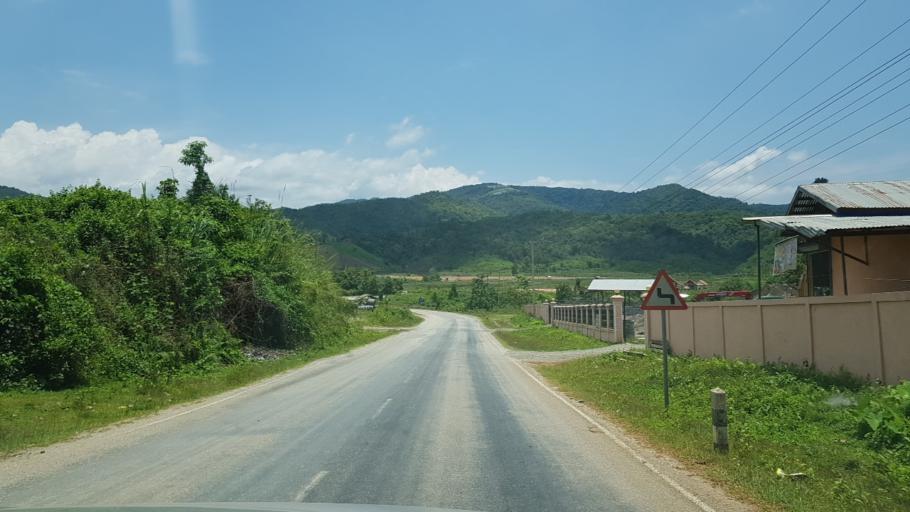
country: LA
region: Vientiane
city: Muang Kasi
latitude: 19.2728
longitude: 102.2166
